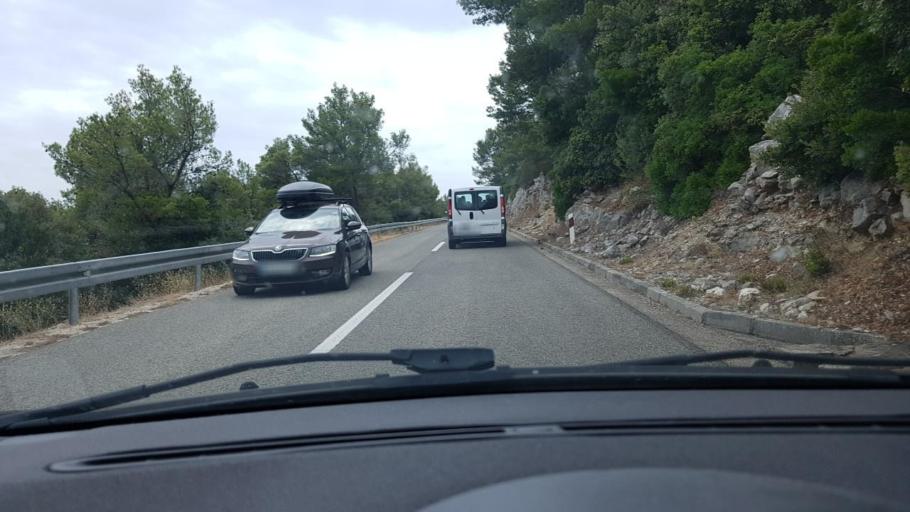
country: HR
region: Dubrovacko-Neretvanska
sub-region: Grad Korcula
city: Zrnovo
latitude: 42.9394
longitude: 17.0237
